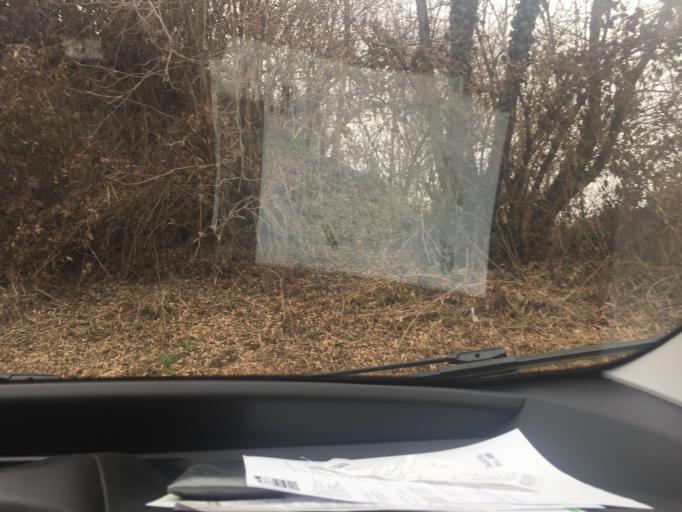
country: IT
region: Piedmont
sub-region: Provincia di Torino
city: Savonera
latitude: 45.0875
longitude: 7.6124
